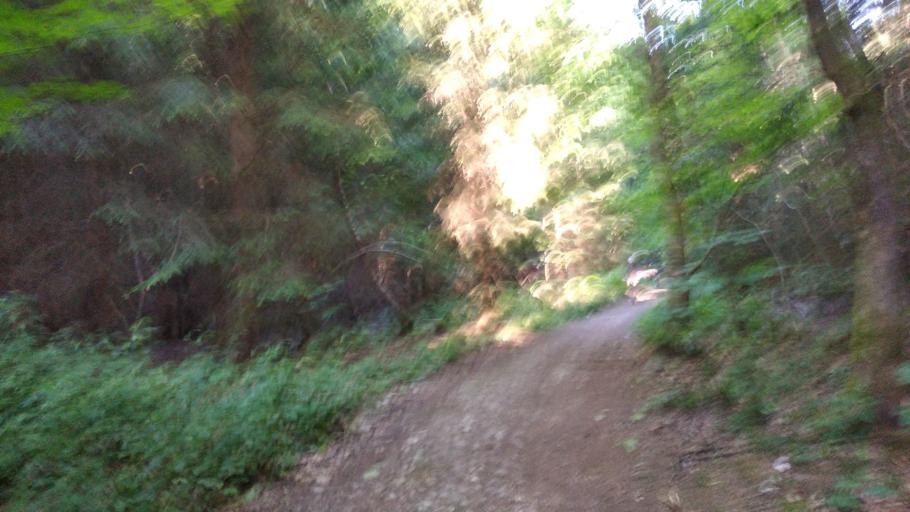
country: DE
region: Bavaria
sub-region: Upper Bavaria
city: Zorneding
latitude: 48.0960
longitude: 11.8073
